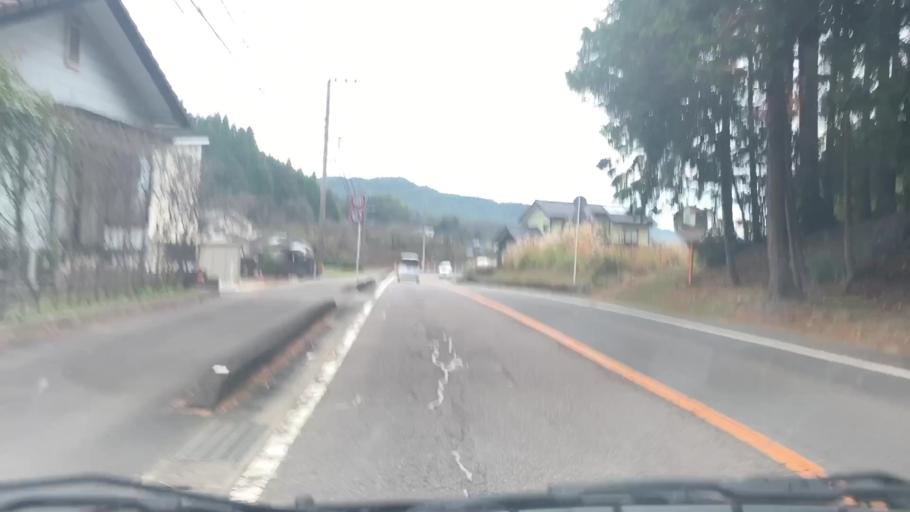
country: JP
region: Saga Prefecture
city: Takeocho-takeo
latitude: 33.1895
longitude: 129.9664
